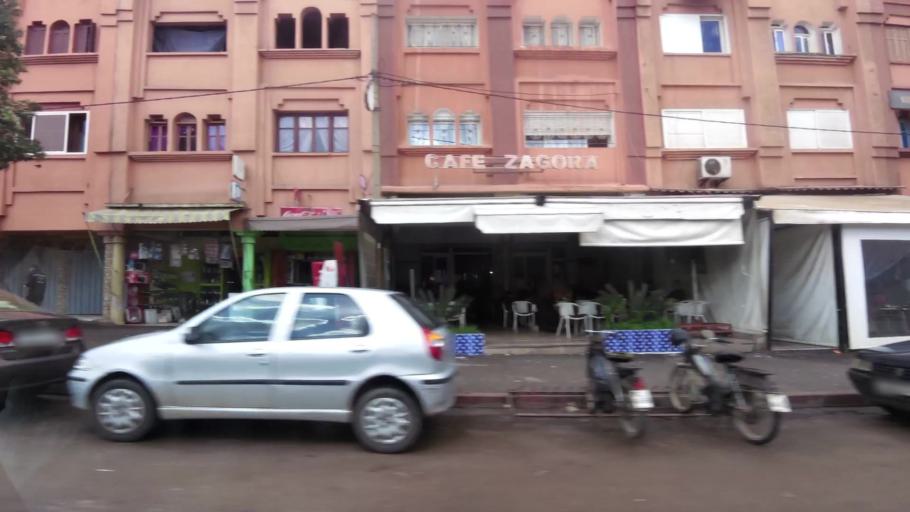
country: MA
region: Grand Casablanca
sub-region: Nouaceur
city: Bouskoura
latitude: 33.5097
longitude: -7.6571
